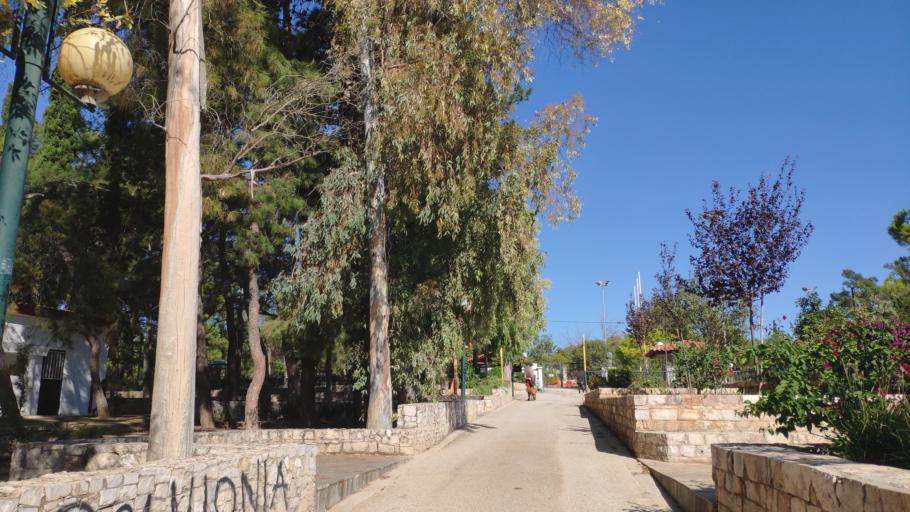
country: GR
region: Attica
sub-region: Nomarchia Athinas
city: Nea Filadelfeia
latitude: 38.0420
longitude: 23.7442
